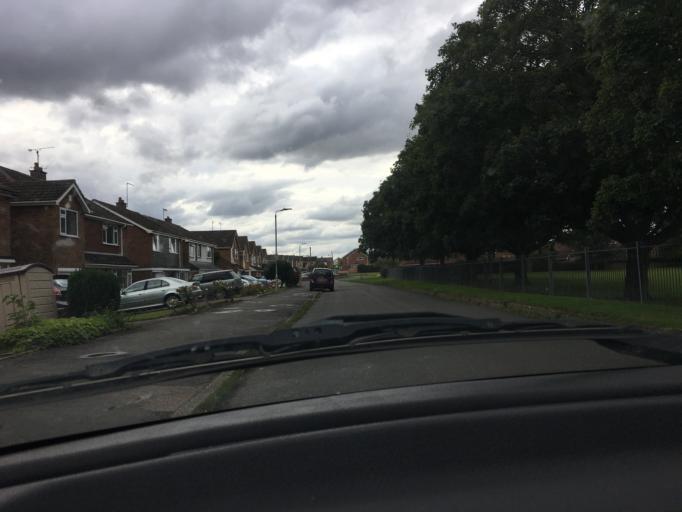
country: GB
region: England
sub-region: Leicestershire
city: Lutterworth
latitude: 52.4571
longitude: -1.2093
